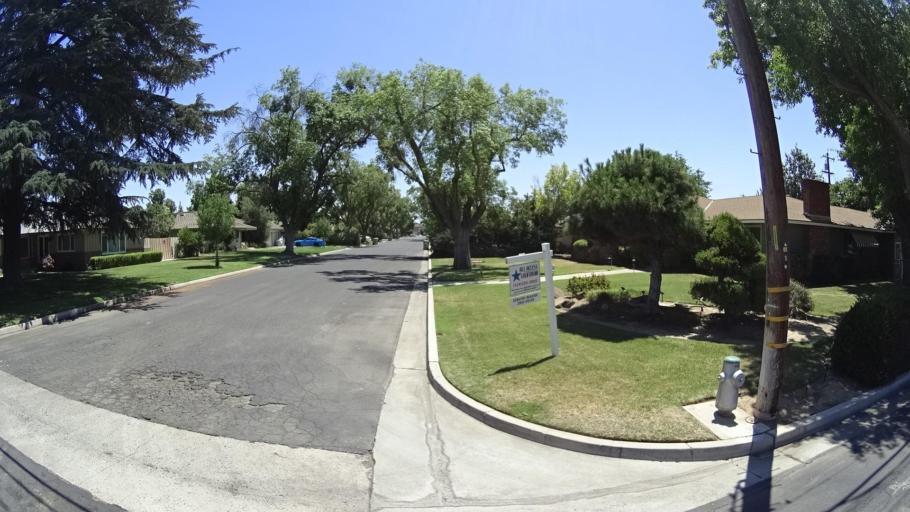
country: US
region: California
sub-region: Fresno County
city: Fresno
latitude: 36.7948
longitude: -119.7950
